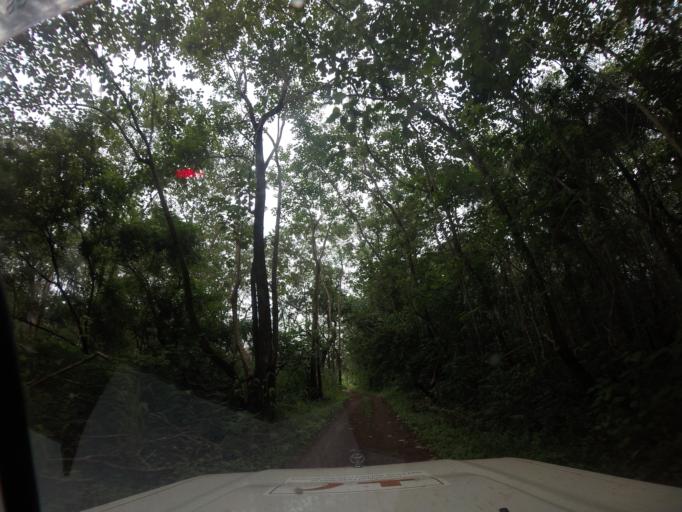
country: SL
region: Northern Province
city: Kamakwie
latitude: 9.6332
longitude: -12.2151
